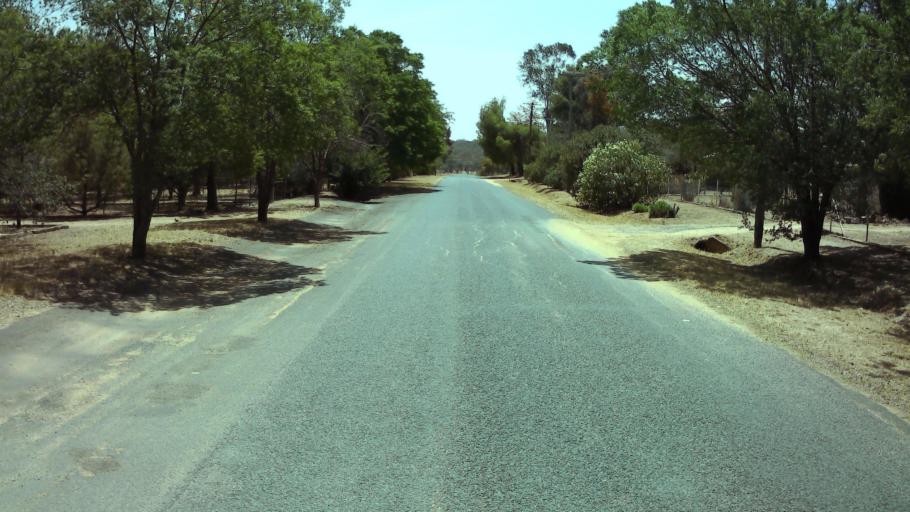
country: AU
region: New South Wales
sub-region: Weddin
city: Grenfell
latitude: -33.8958
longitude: 148.1721
